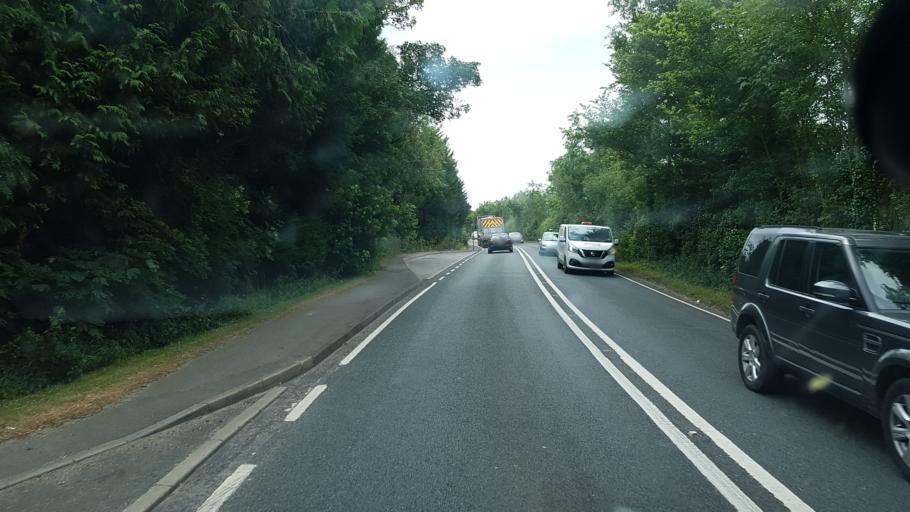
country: GB
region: England
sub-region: Surrey
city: Godstone
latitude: 51.2319
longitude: -0.0481
